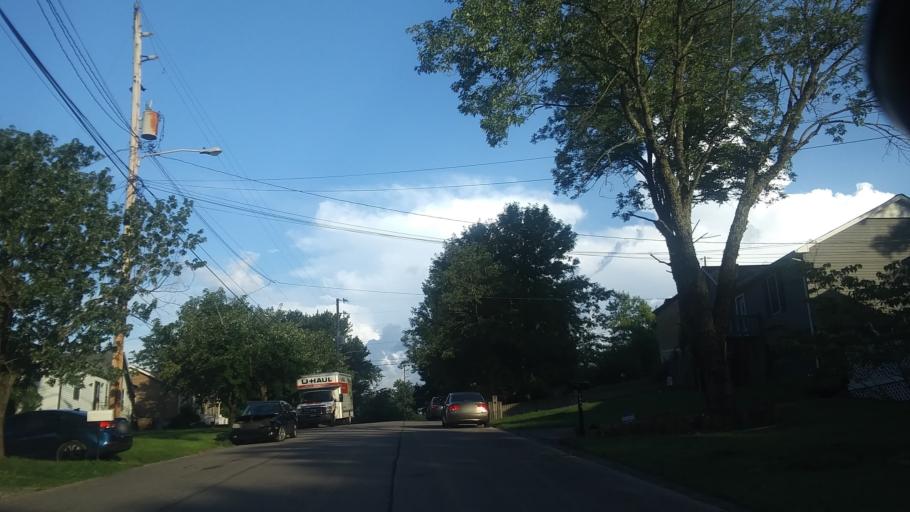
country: US
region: Tennessee
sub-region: Rutherford County
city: La Vergne
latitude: 36.0748
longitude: -86.6701
